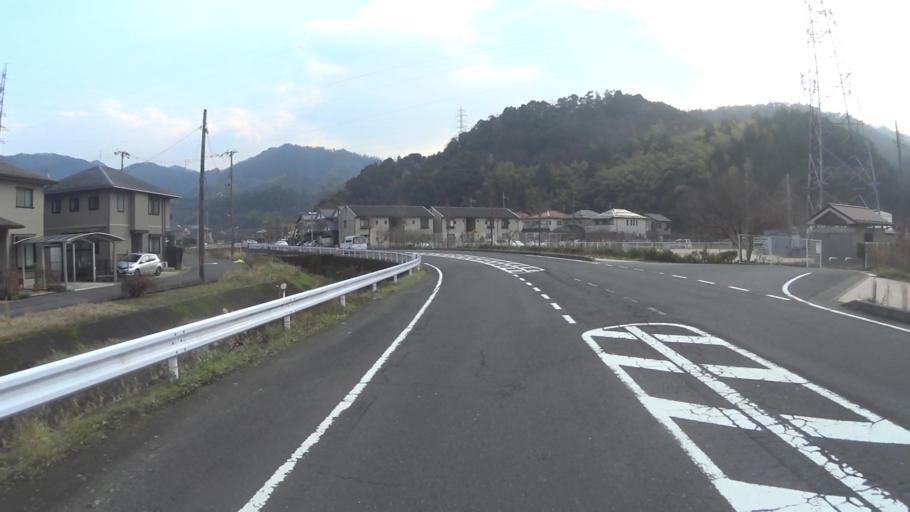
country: JP
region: Kyoto
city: Maizuru
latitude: 35.4525
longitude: 135.3971
